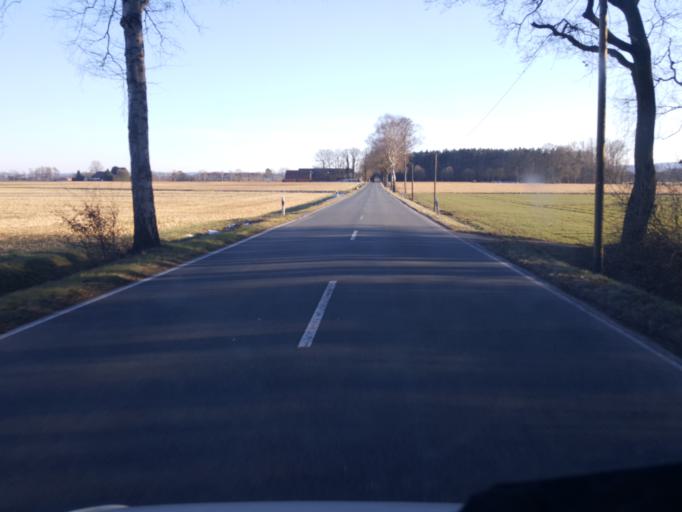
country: DE
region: North Rhine-Westphalia
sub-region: Regierungsbezirk Detmold
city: Hille
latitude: 52.3805
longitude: 8.7259
